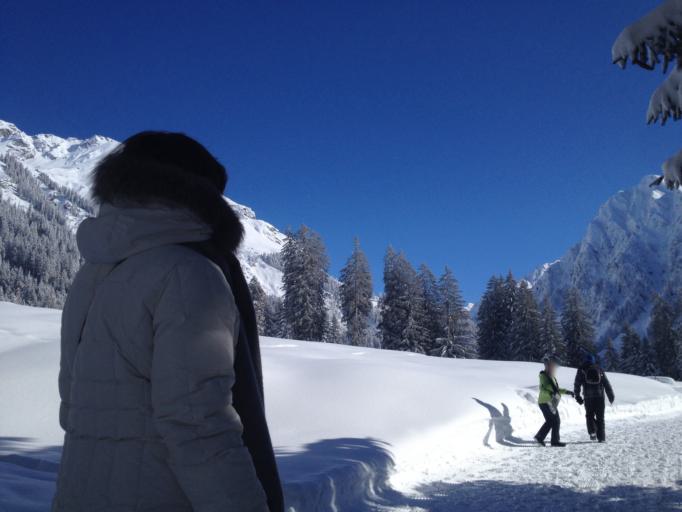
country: CH
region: Grisons
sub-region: Praettigau/Davos District
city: Klosters Serneus
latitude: 46.8598
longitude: 9.9403
